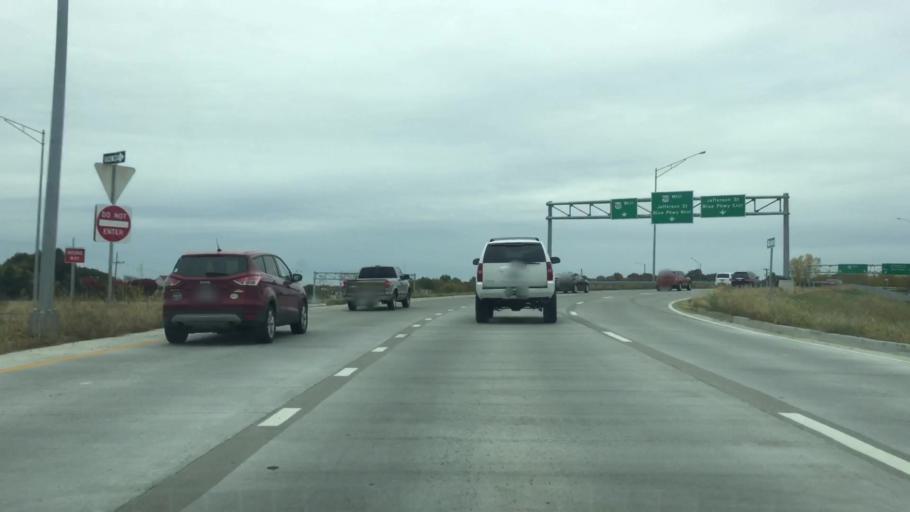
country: US
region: Missouri
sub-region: Jackson County
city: Lees Summit
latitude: 38.9021
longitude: -94.3769
